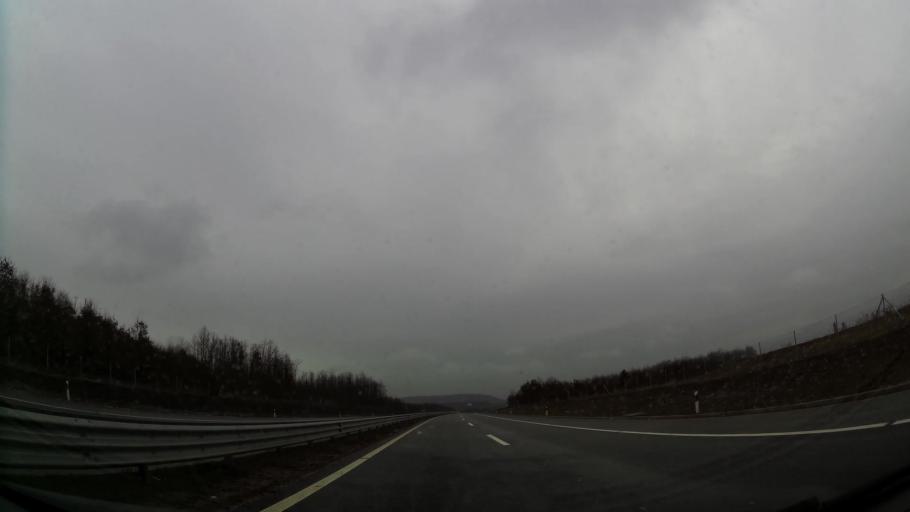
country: XK
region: Ferizaj
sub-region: Komuna e Ferizajt
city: Ferizaj
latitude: 42.3482
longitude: 21.2054
